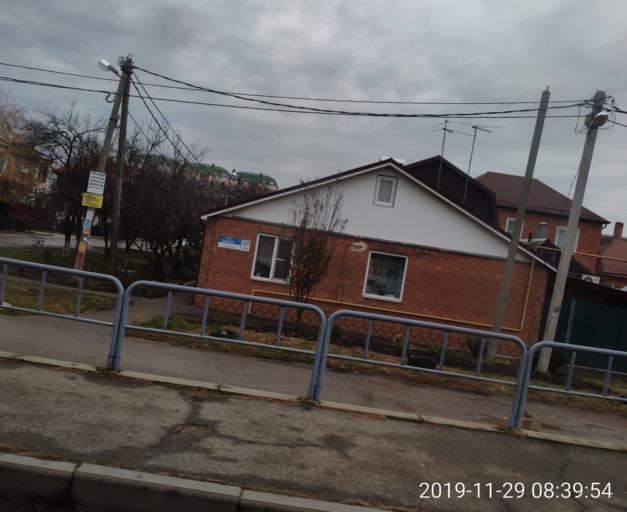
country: RU
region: Krasnodarskiy
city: Krasnodar
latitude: 45.0469
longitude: 38.9965
